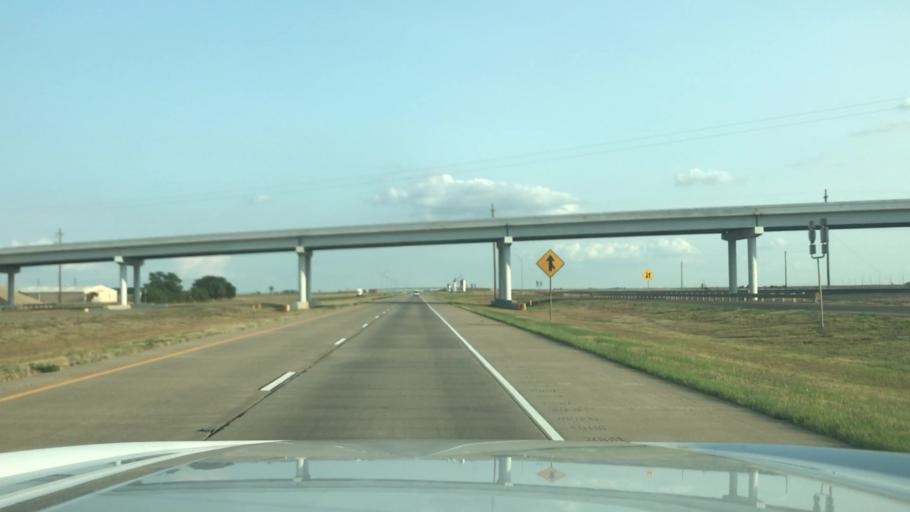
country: US
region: Texas
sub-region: Swisher County
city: Tulia
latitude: 34.6476
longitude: -101.8266
